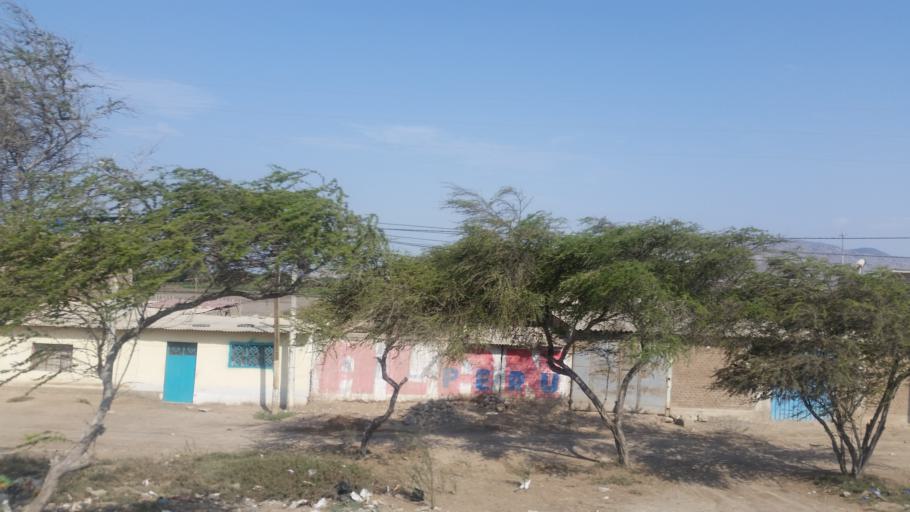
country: PE
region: Lambayeque
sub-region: Provincia de Chiclayo
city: Reque
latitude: -6.8413
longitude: -79.8293
